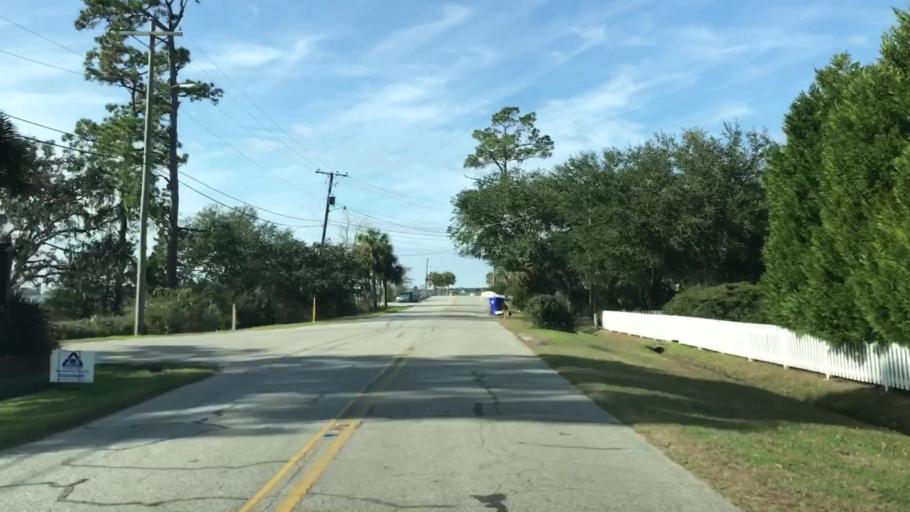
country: US
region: South Carolina
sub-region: Charleston County
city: Charleston
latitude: 32.7719
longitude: -80.0056
